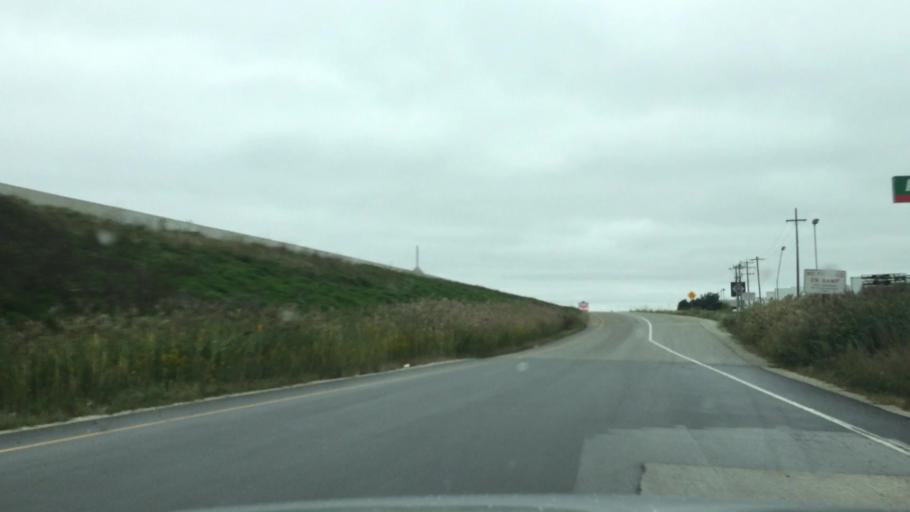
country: US
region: Wisconsin
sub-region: Racine County
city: Franksville
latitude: 42.7254
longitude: -87.9546
